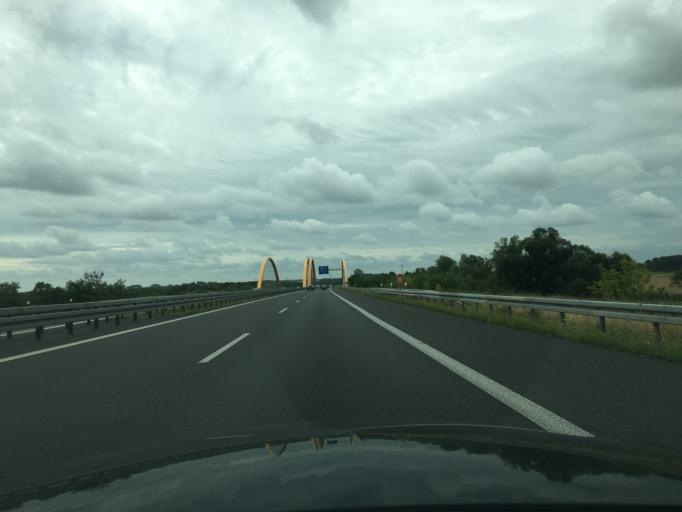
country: DE
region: Brandenburg
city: Brieselang
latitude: 52.5886
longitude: 12.9715
